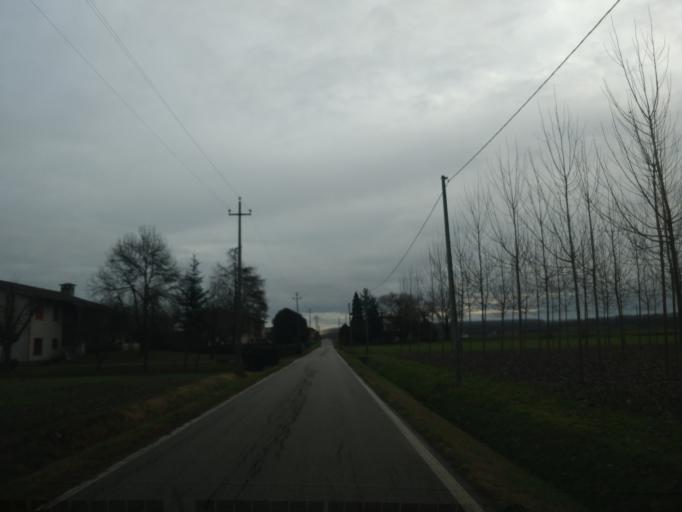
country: IT
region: Emilia-Romagna
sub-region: Provincia di Ferrara
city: Corpo Reno
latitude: 44.7565
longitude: 11.3190
